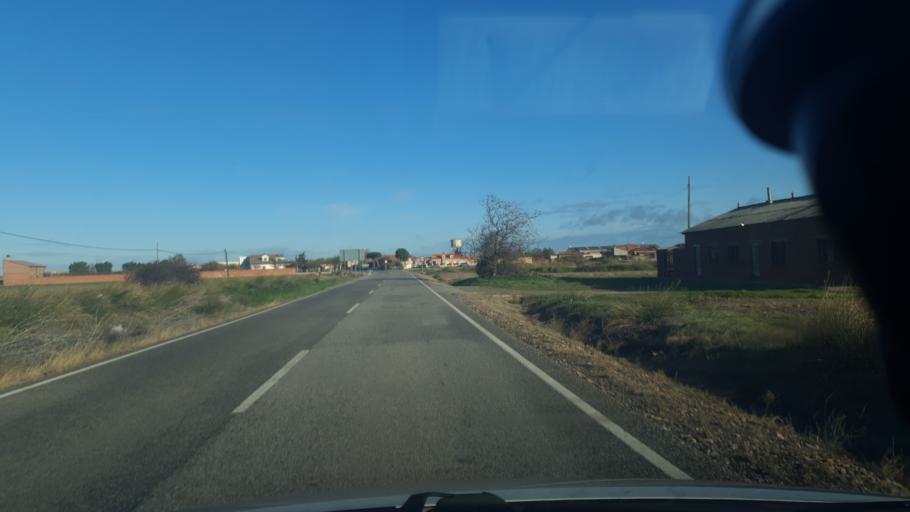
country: ES
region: Castille and Leon
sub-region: Provincia de Avila
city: Tinosillos
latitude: 40.9278
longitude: -4.7275
